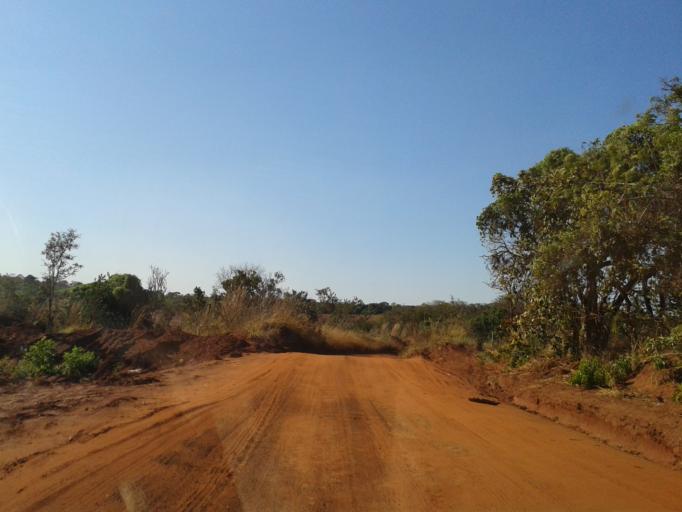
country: BR
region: Minas Gerais
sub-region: Ituiutaba
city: Ituiutaba
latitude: -19.0196
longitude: -49.3542
